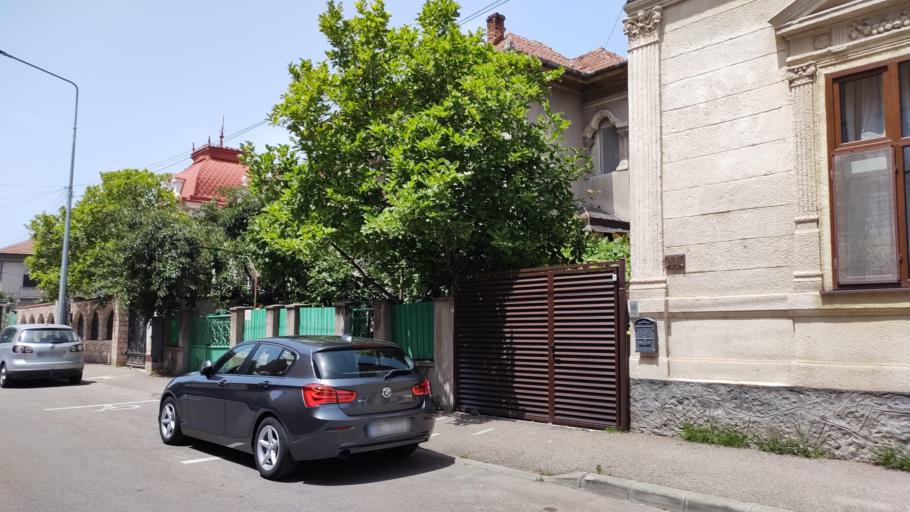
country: RO
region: Mehedinti
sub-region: Municipiul Drobeta-Turnu Severin
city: Drobeta-Turnu Severin
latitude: 44.6246
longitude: 22.6657
